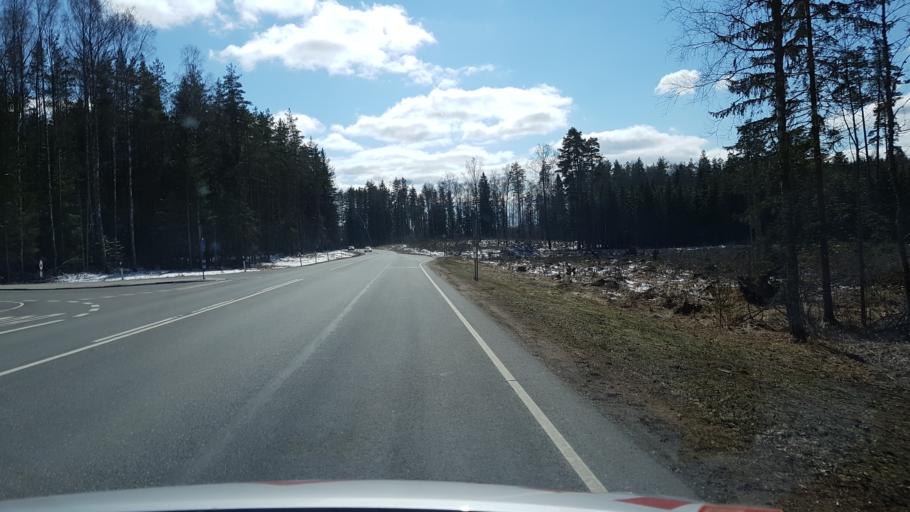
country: EE
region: Laeaene-Virumaa
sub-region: Kadrina vald
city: Kadrina
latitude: 59.3953
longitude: 26.0134
